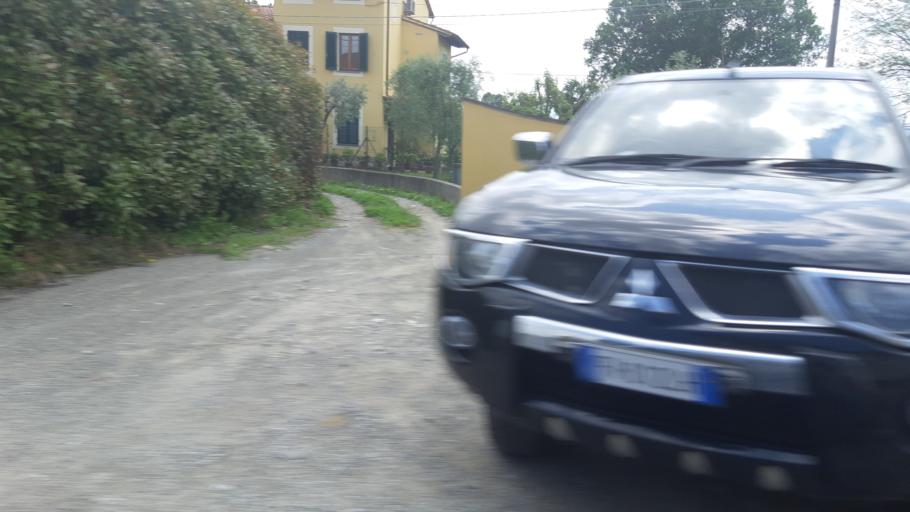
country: IT
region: Tuscany
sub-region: Provincia di Lucca
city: Capannori
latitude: 43.8615
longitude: 10.5503
